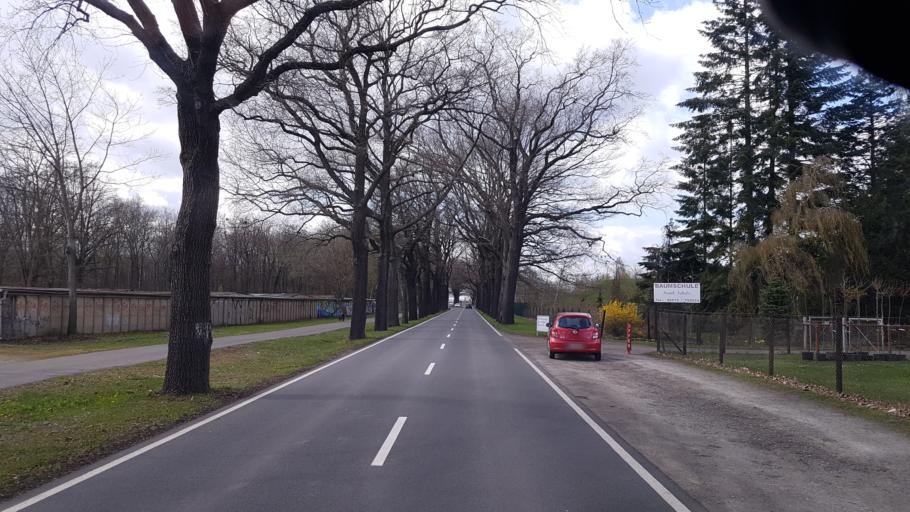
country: DE
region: Brandenburg
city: Senftenberg
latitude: 51.5236
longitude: 13.9767
